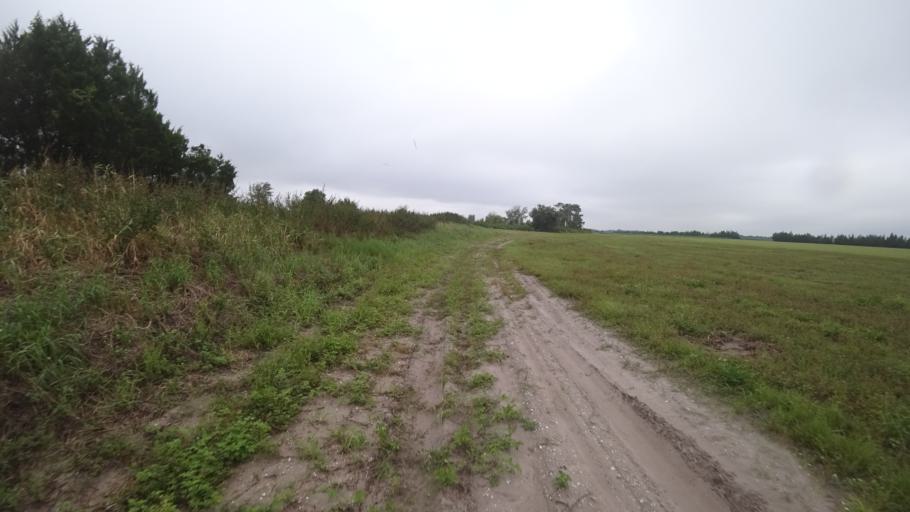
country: US
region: Florida
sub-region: Sarasota County
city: Warm Mineral Springs
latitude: 27.3047
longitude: -82.1474
